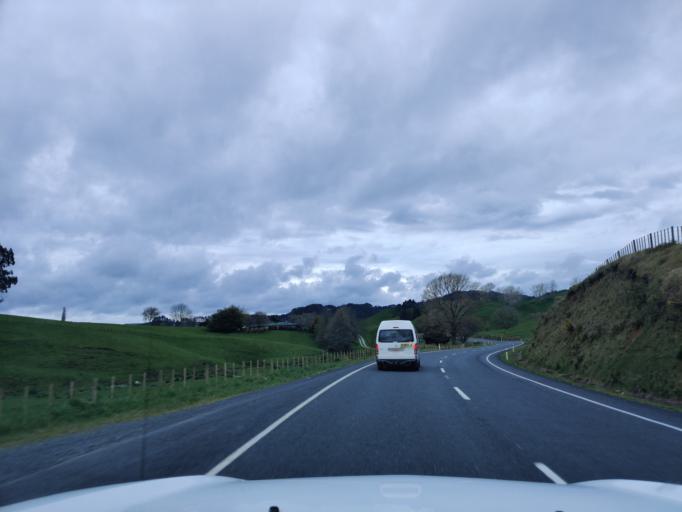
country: NZ
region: Waikato
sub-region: Otorohanga District
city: Otorohanga
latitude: -38.4536
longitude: 175.1640
